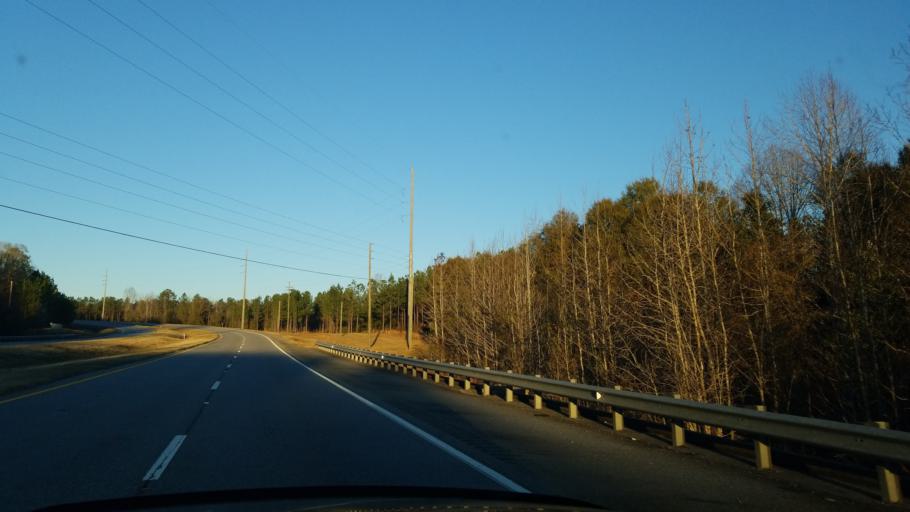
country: US
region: Georgia
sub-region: Chattahoochee County
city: Cusseta
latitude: 32.2720
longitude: -84.7838
